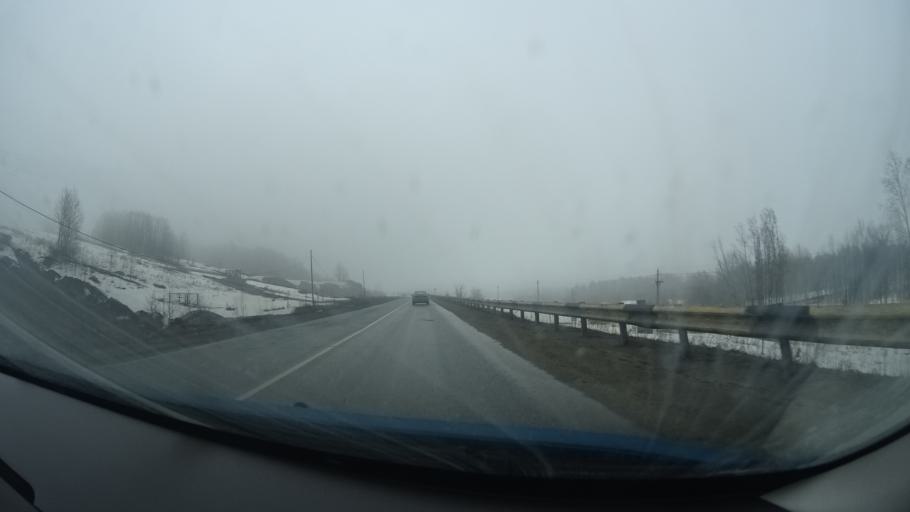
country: RU
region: Perm
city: Kuyeda
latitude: 56.4599
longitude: 55.6357
